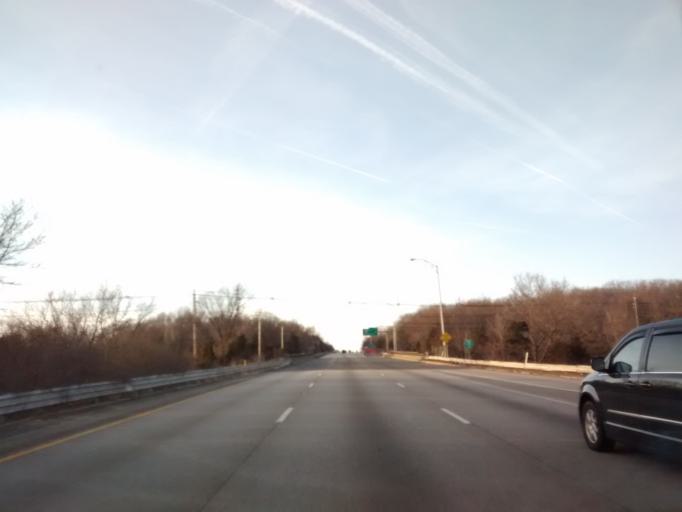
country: US
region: Massachusetts
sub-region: Worcester County
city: Southborough
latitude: 42.2878
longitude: -71.5663
